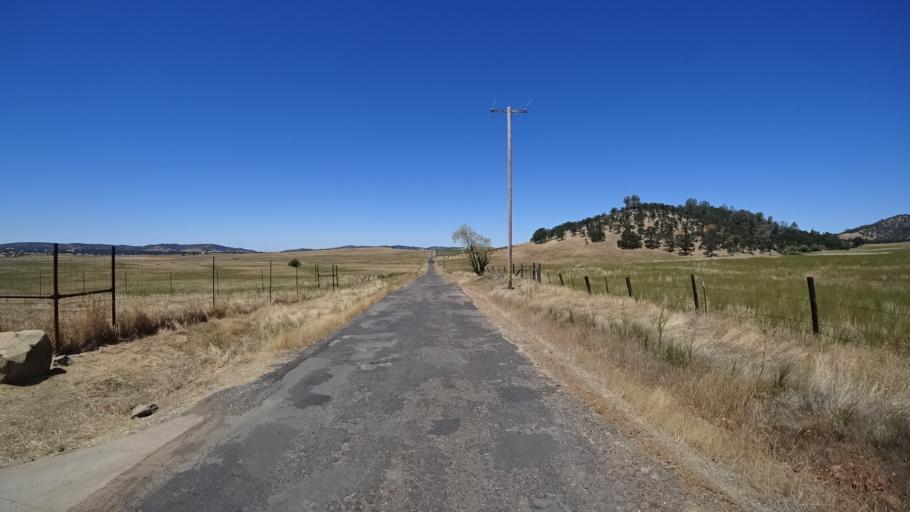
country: US
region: California
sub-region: Calaveras County
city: Copperopolis
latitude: 38.0482
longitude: -120.6973
